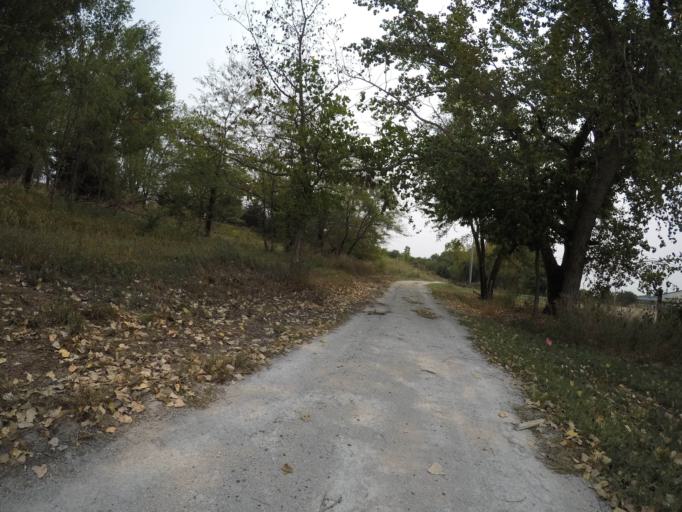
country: US
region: Kansas
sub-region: Marshall County
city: Marysville
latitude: 39.8603
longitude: -96.6527
